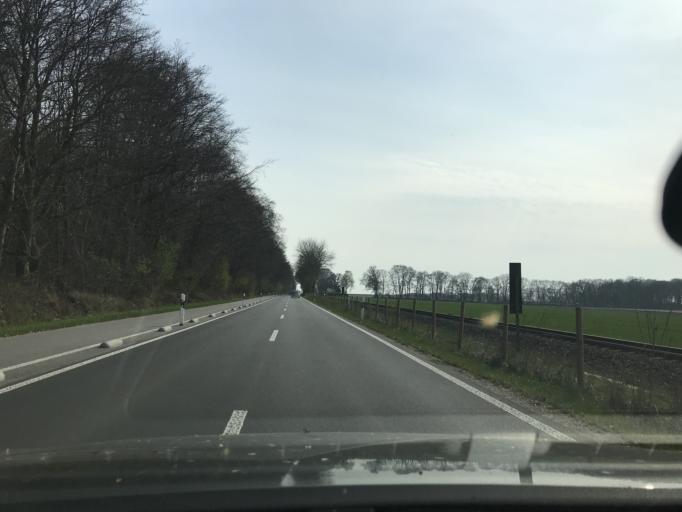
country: DE
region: North Rhine-Westphalia
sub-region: Regierungsbezirk Dusseldorf
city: Kleve
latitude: 51.7394
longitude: 6.1675
